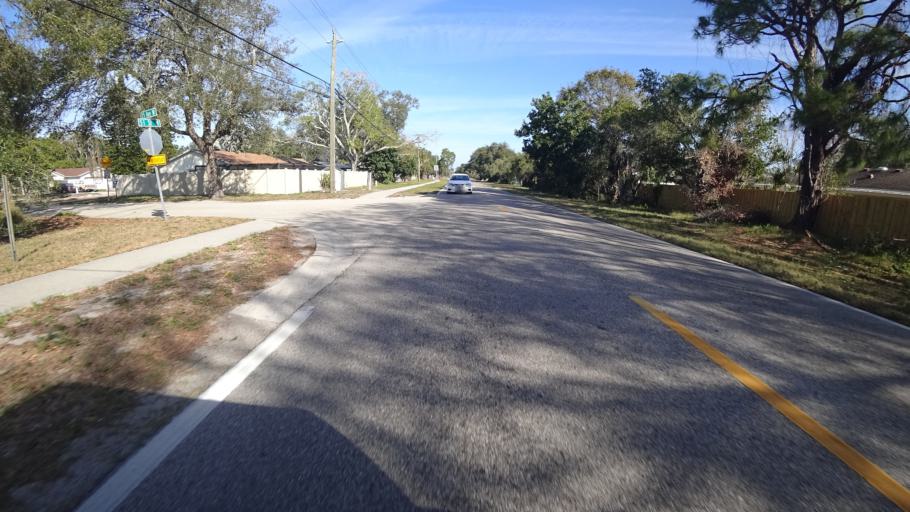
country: US
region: Florida
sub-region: Manatee County
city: South Bradenton
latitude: 27.4700
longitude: -82.6123
